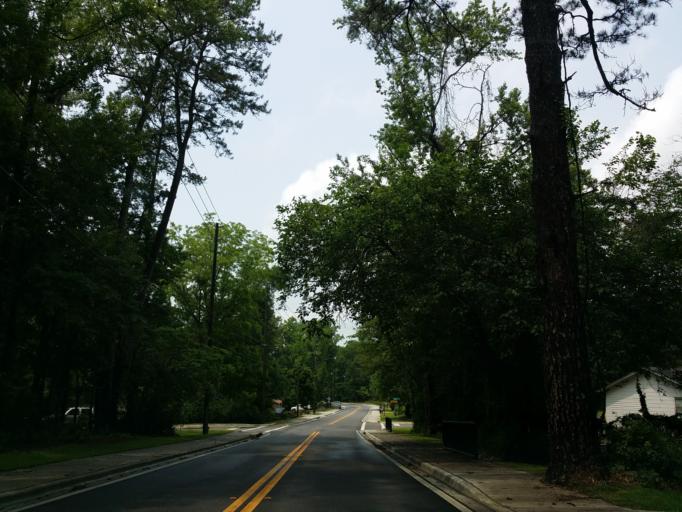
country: US
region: Florida
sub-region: Leon County
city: Tallahassee
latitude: 30.4871
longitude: -84.2314
